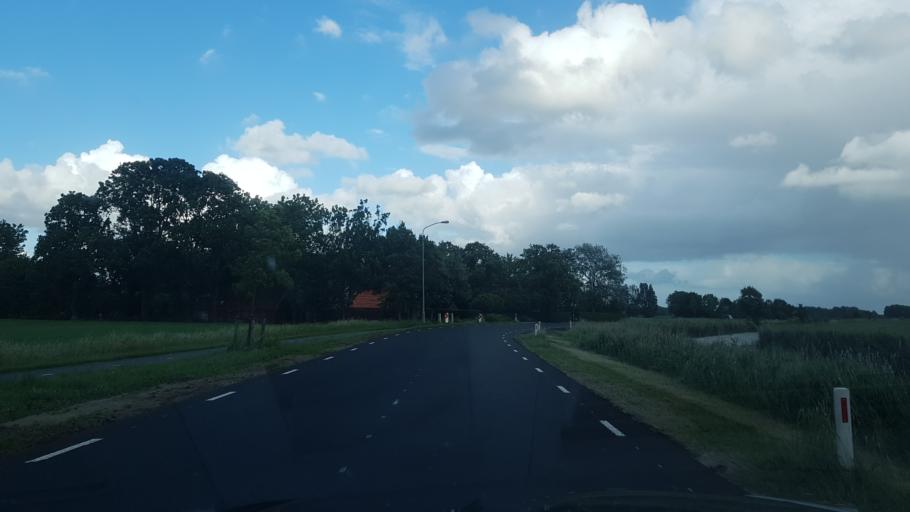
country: NL
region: Groningen
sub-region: Gemeente Appingedam
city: Appingedam
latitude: 53.3236
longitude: 6.7597
